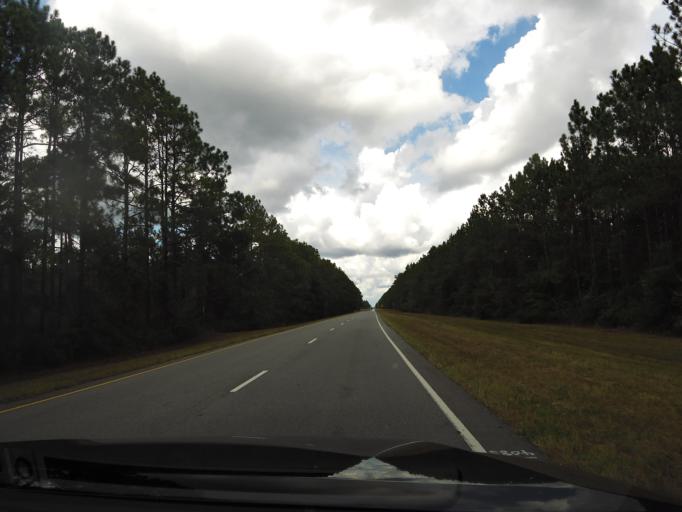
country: US
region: Georgia
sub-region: Charlton County
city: Folkston
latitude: 30.8719
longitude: -82.0128
